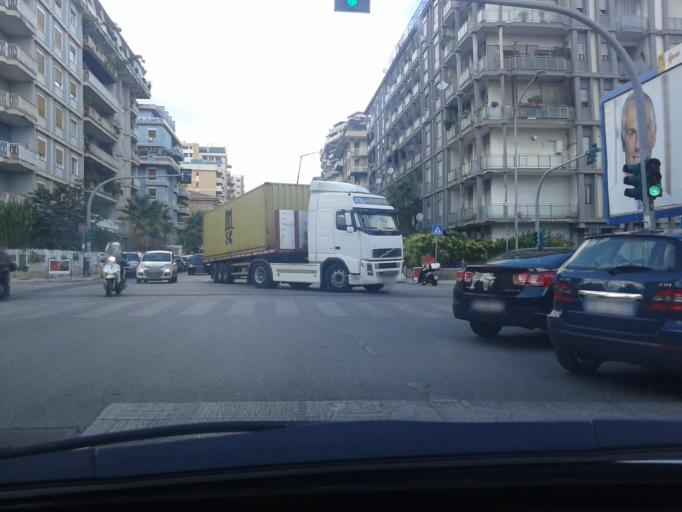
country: IT
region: Sicily
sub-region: Palermo
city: Palermo
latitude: 38.1478
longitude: 13.3305
